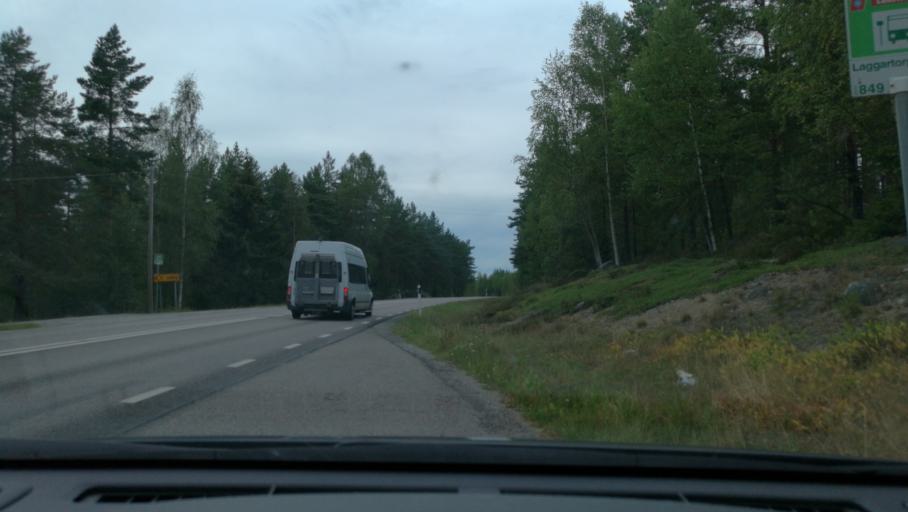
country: SE
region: Soedermanland
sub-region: Katrineholms Kommun
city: Katrineholm
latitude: 59.1337
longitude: 16.1389
